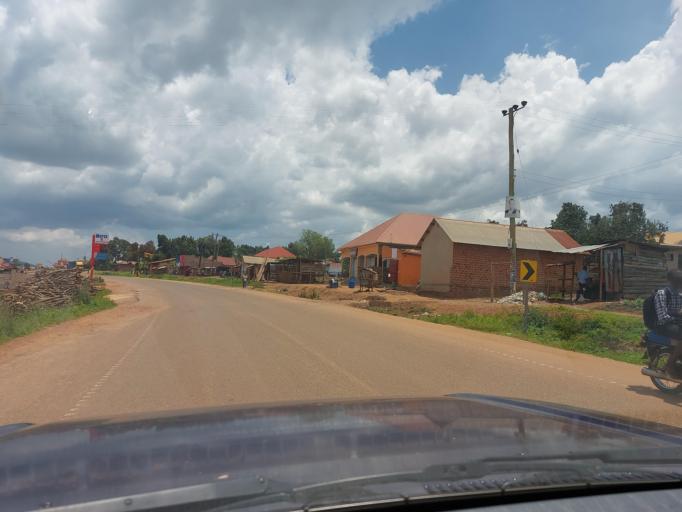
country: UG
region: Central Region
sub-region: Mukono District
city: Mukono
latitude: 0.3025
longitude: 32.7770
